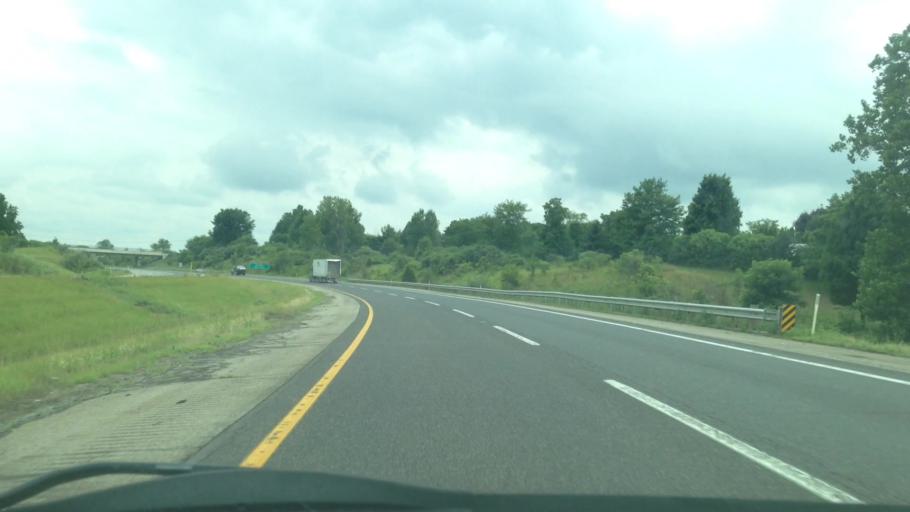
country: US
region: Indiana
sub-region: Steuben County
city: Fremont
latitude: 41.7347
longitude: -84.9758
